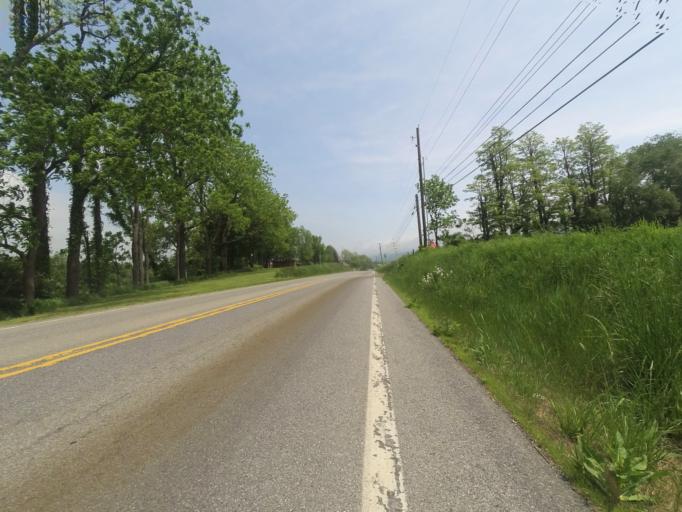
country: US
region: Pennsylvania
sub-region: Centre County
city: Stormstown
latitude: 40.7030
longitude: -77.9906
